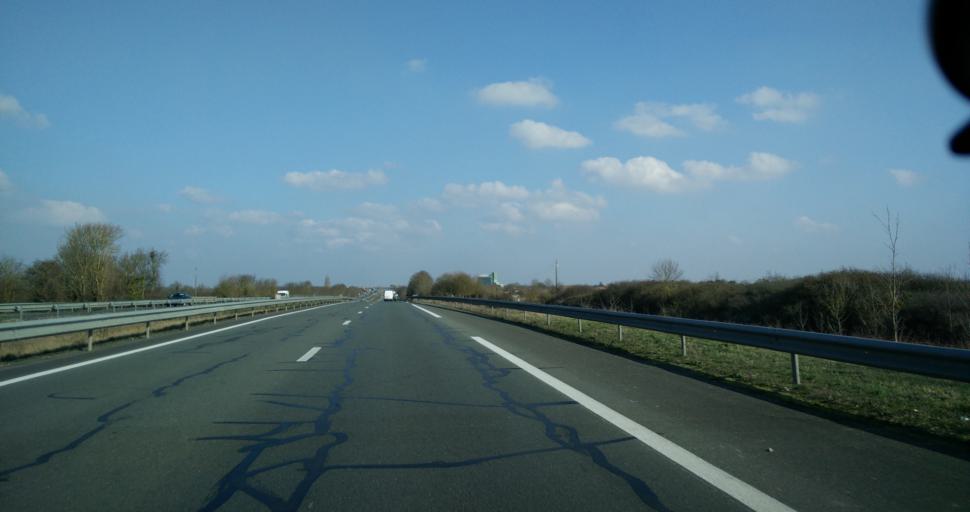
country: FR
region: Poitou-Charentes
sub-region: Departement de la Charente-Maritime
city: Sainte-Soulle
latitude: 46.2098
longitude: -1.0043
